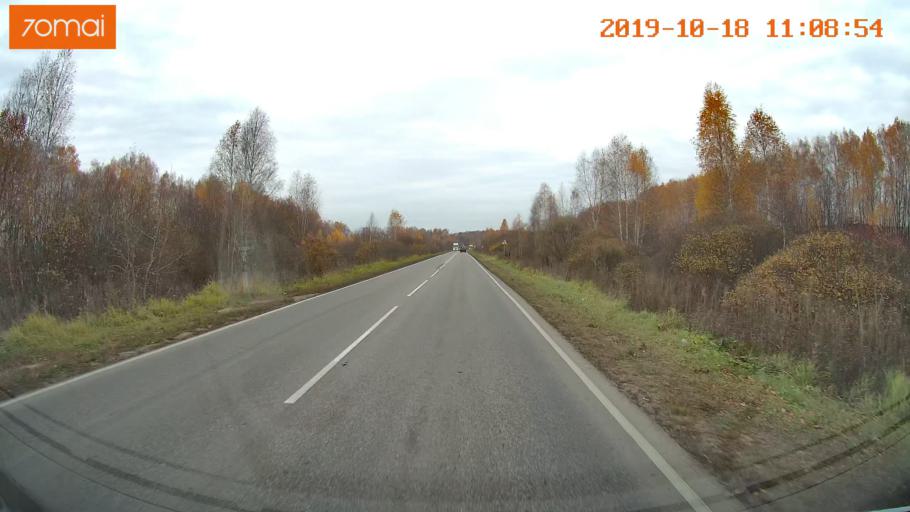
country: RU
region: Tula
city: Kimovsk
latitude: 53.9454
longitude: 38.5341
